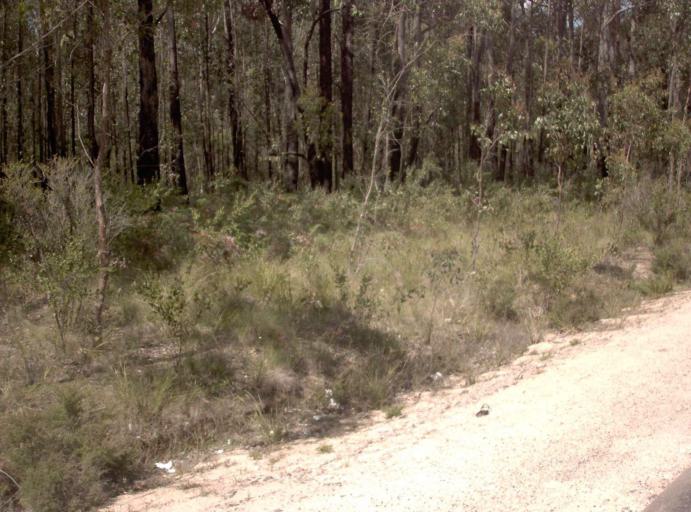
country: AU
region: New South Wales
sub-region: Bombala
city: Bombala
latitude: -37.5440
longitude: 149.4229
